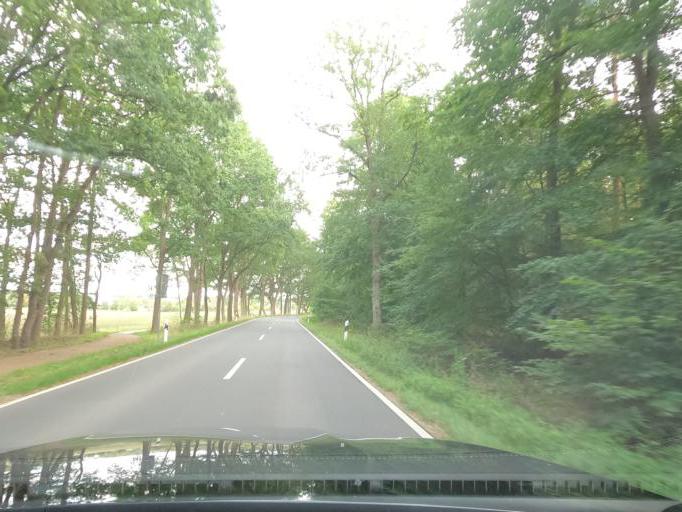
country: DE
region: Lower Saxony
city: Isernhagen Farster Bauerschaft
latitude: 52.5138
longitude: 9.9018
